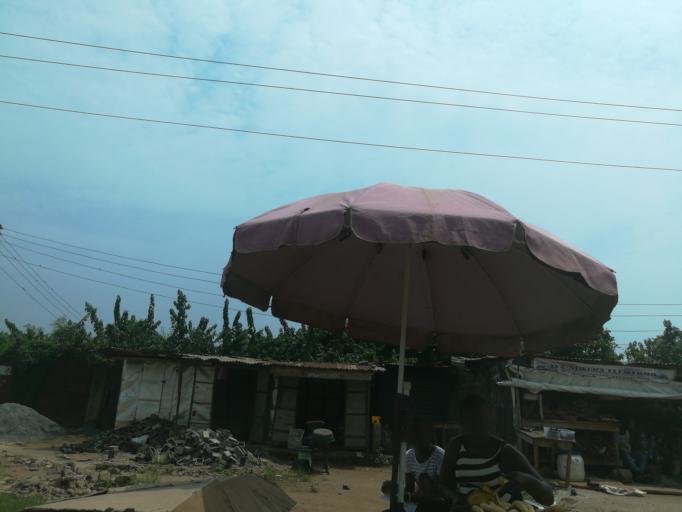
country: NG
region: Lagos
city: Ikorodu
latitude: 6.6037
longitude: 3.6049
